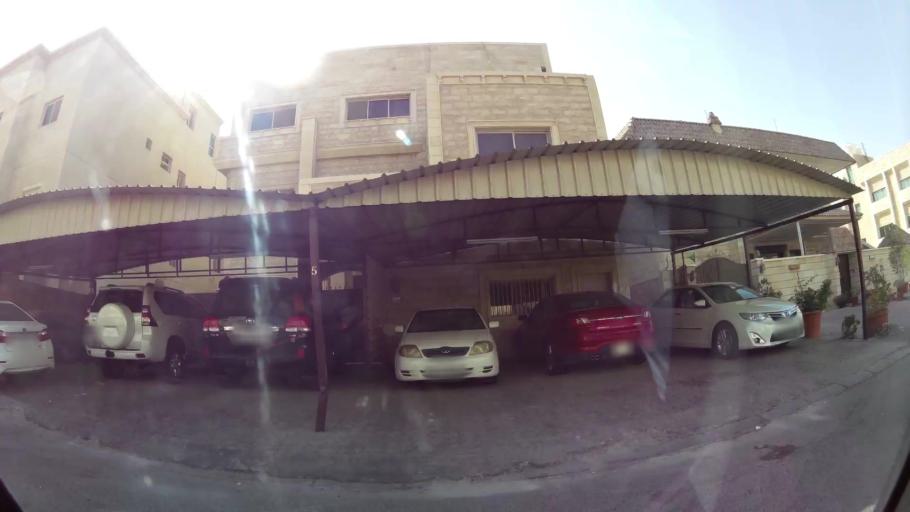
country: KW
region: Muhafazat Hawalli
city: Salwa
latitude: 29.2887
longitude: 48.0788
